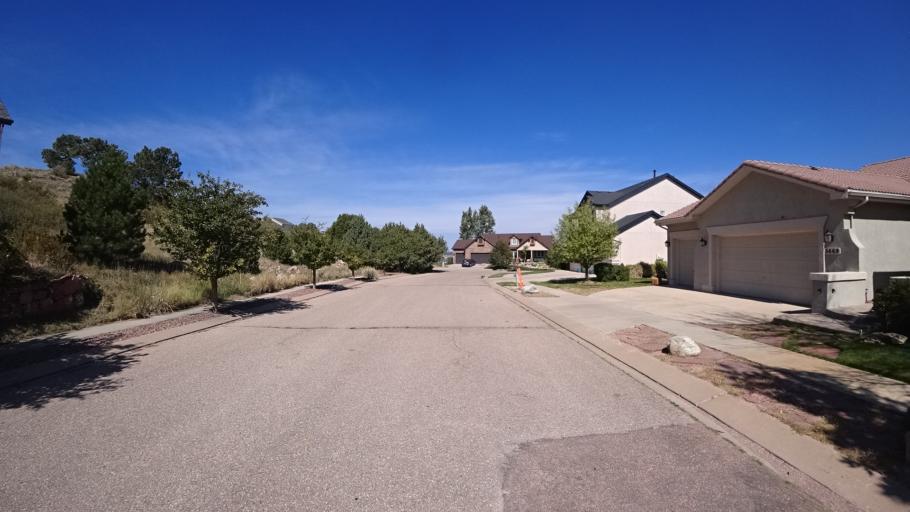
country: US
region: Colorado
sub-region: El Paso County
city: Cimarron Hills
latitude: 38.9151
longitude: -104.7430
